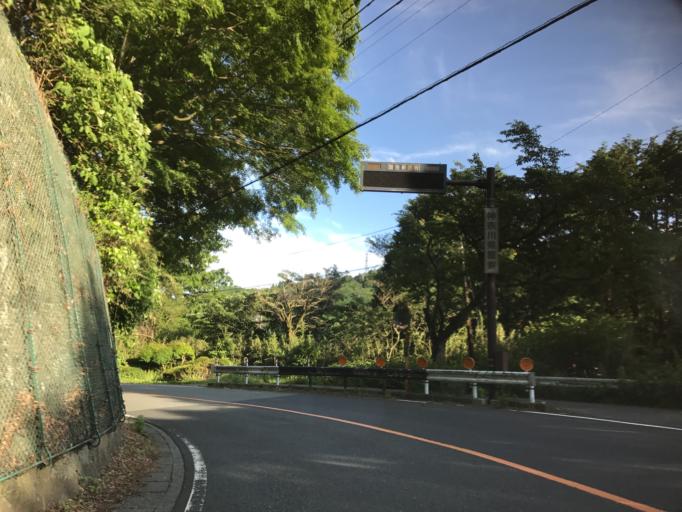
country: JP
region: Kanagawa
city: Hakone
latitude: 35.2582
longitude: 139.0405
